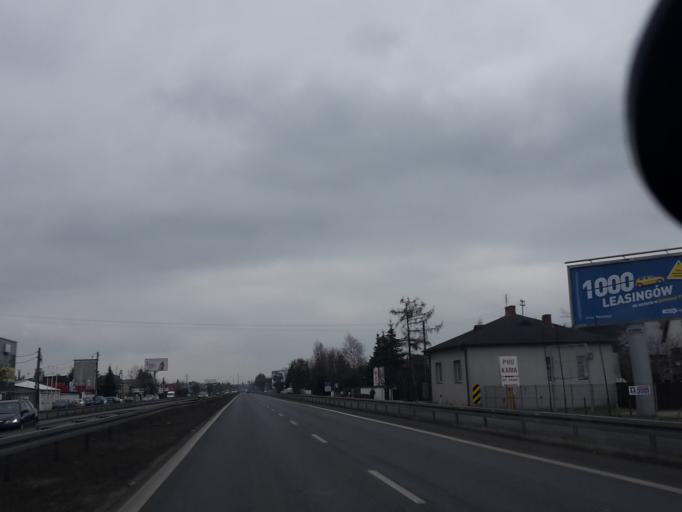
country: PL
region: Masovian Voivodeship
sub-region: Powiat warszawski zachodni
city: Lomianki
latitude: 52.3382
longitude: 20.8743
